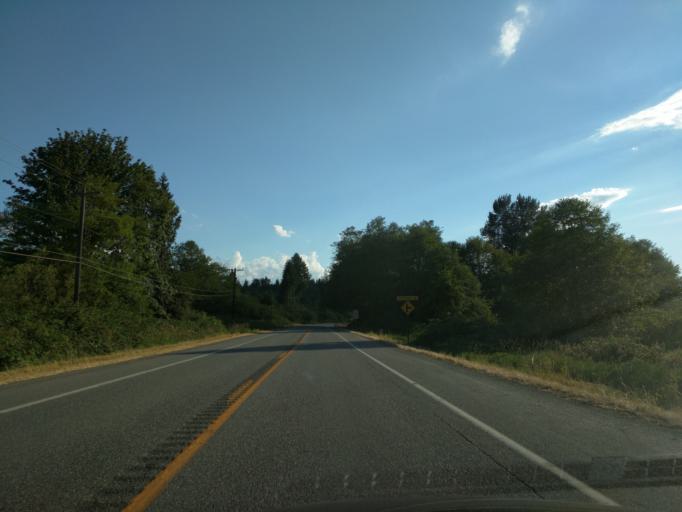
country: US
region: Washington
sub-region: Snohomish County
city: Arlington Heights
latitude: 48.2485
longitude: -122.0403
